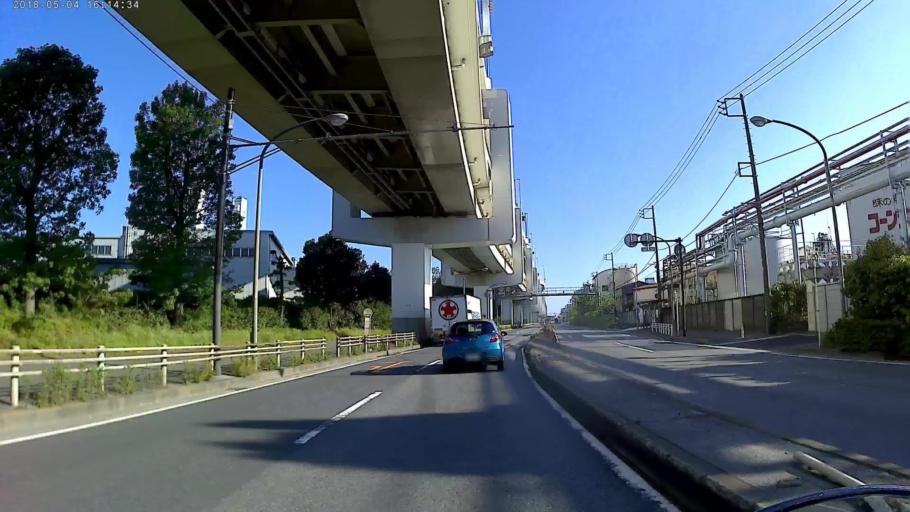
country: JP
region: Kanagawa
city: Yokohama
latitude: 35.4813
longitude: 139.6753
